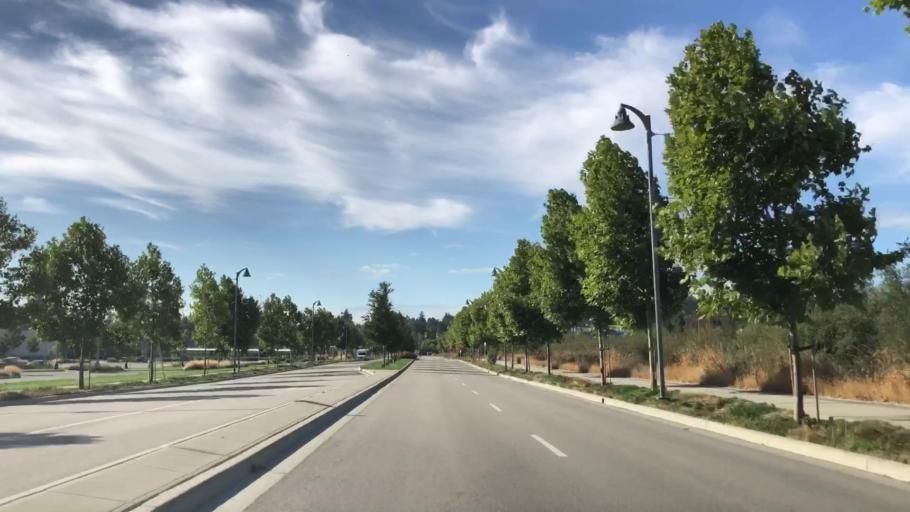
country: CA
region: British Columbia
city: Ladner
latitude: 49.0372
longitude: -123.0903
